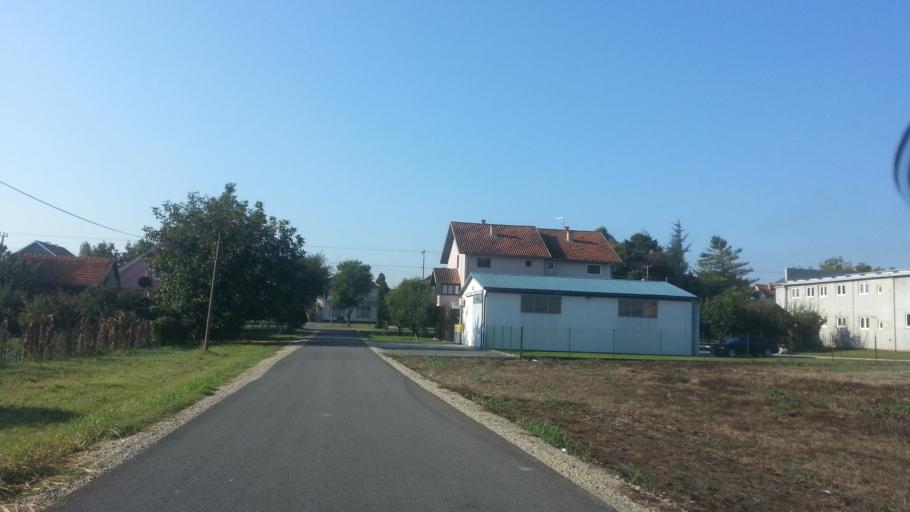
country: RS
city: Stari Banovci
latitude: 44.9863
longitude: 20.2677
